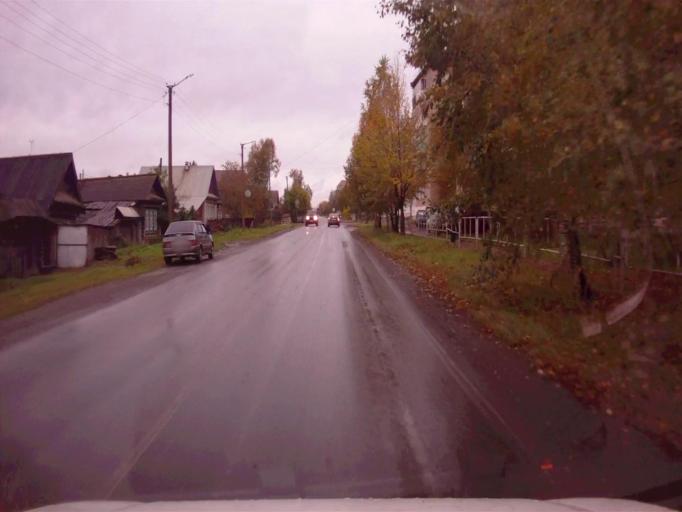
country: RU
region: Chelyabinsk
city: Verkhniy Ufaley
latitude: 56.0497
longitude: 60.2209
